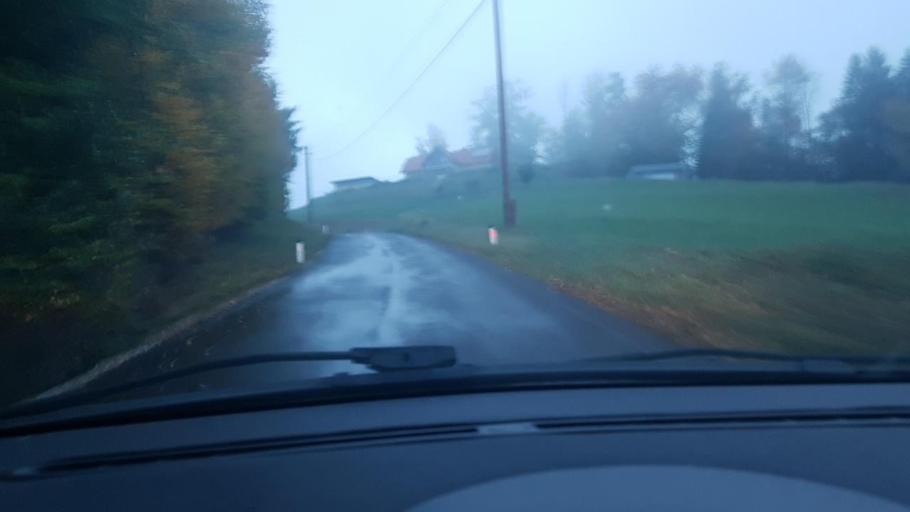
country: AT
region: Styria
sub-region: Politischer Bezirk Leibnitz
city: Sulztal an der Weinstrasse
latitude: 46.6610
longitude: 15.5408
